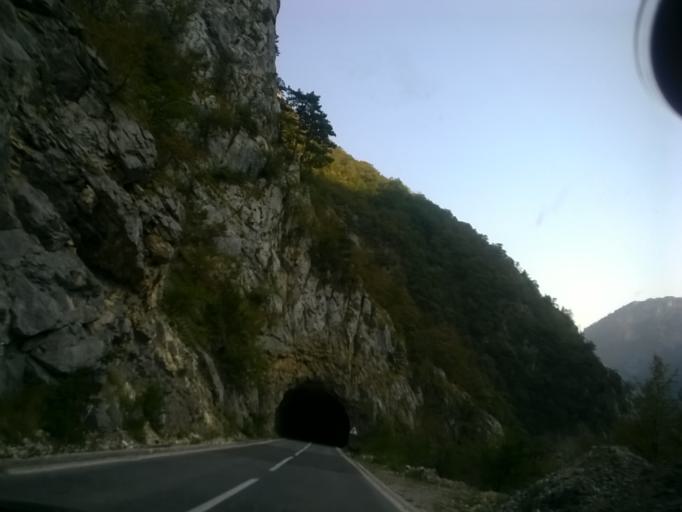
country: ME
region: Opstina Pluzine
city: Pluzine
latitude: 43.2349
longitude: 18.8451
